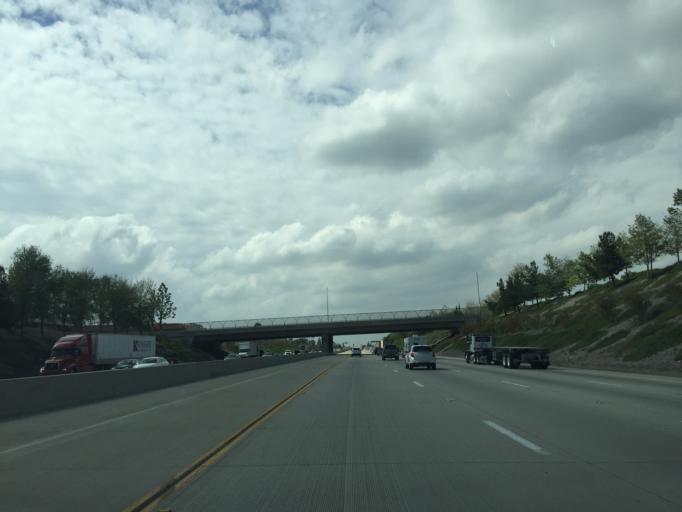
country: US
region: California
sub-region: Los Angeles County
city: La Verne
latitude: 34.1196
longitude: -117.7751
